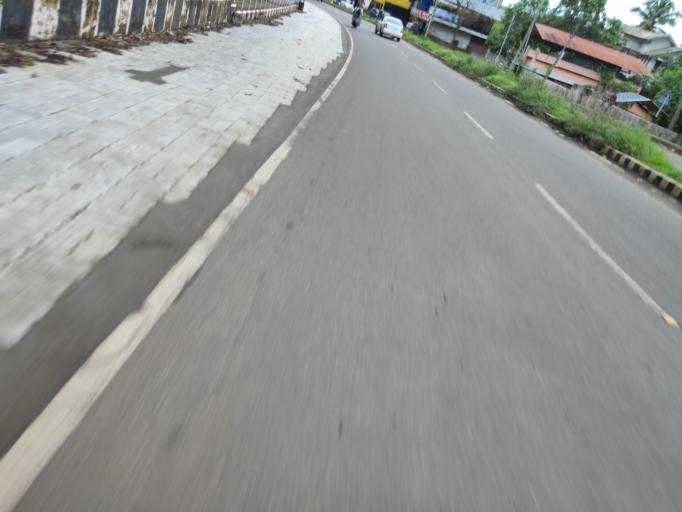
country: IN
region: Kerala
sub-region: Malappuram
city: Manjeri
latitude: 11.1966
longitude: 76.2278
